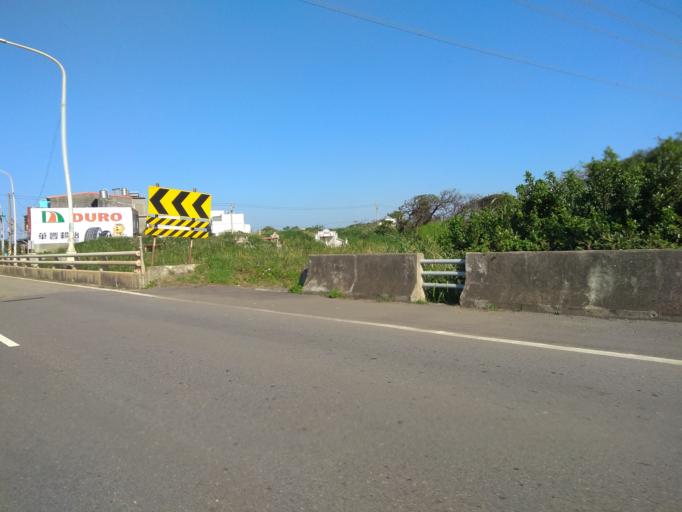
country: TW
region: Taiwan
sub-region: Hsinchu
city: Zhubei
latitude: 25.0155
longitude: 121.0512
